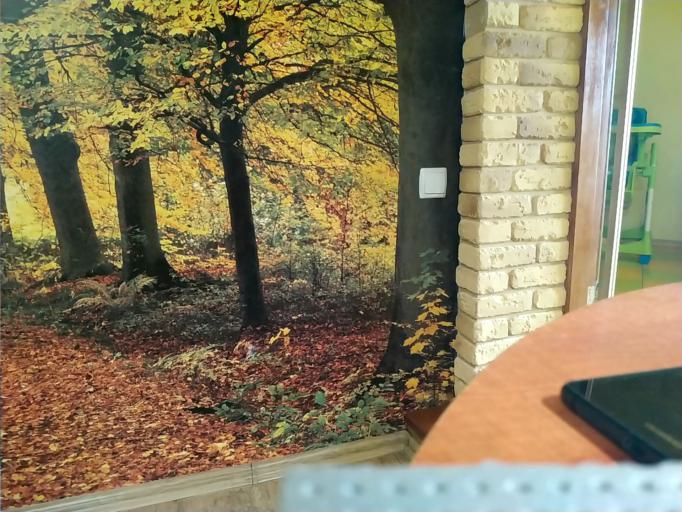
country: RU
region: Tverskaya
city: Kalashnikovo
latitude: 57.2672
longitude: 35.1344
